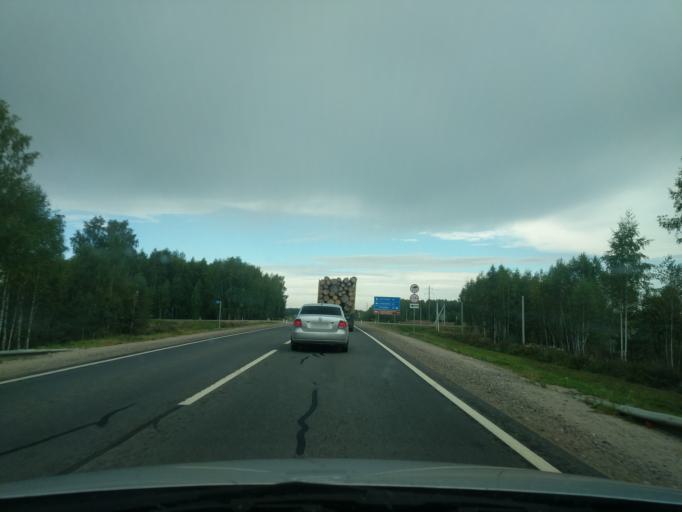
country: RU
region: Kostroma
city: Ostrovskoye
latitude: 57.8081
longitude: 42.2920
